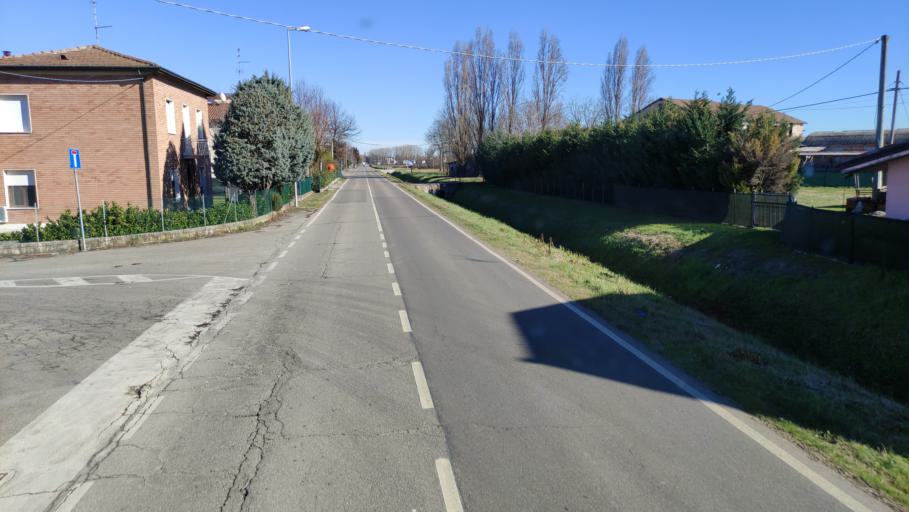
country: IT
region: Emilia-Romagna
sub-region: Provincia di Reggio Emilia
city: Prato
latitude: 44.7249
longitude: 10.7662
